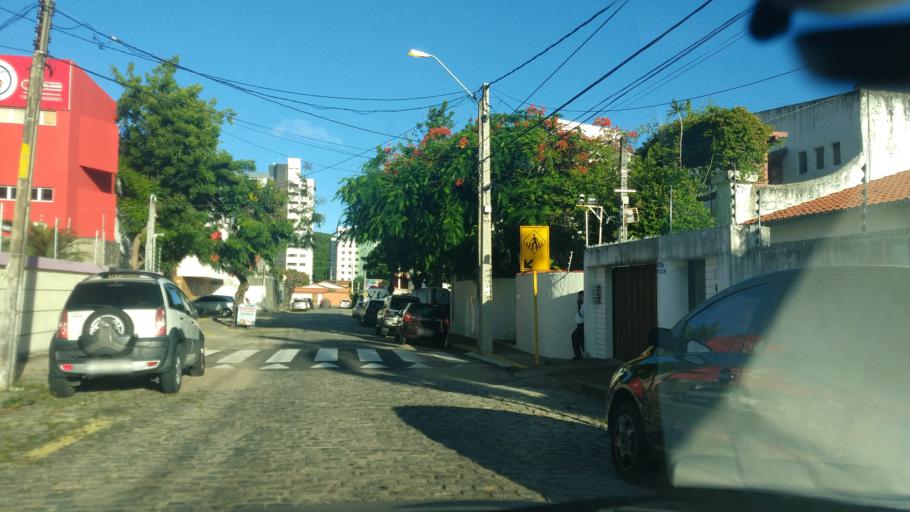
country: BR
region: Rio Grande do Norte
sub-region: Natal
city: Natal
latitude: -5.8131
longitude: -35.2002
